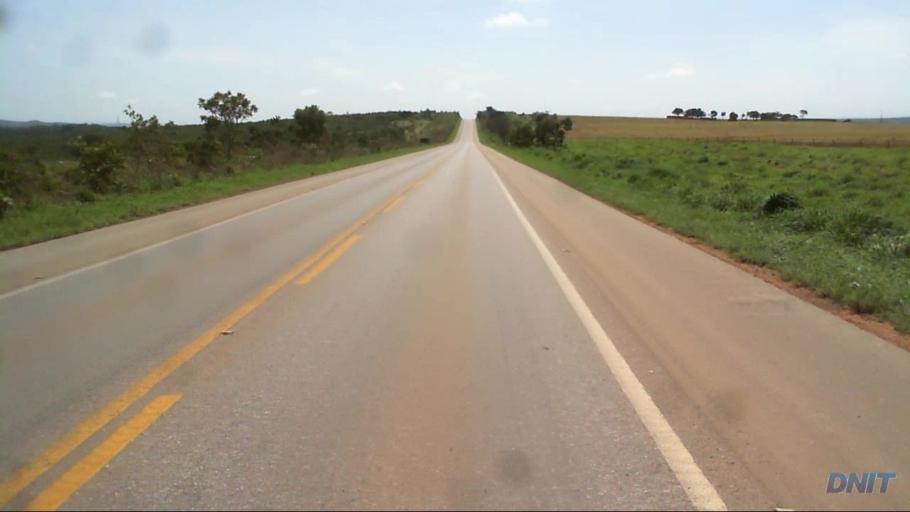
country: BR
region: Goias
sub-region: Barro Alto
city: Barro Alto
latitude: -15.2064
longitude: -48.7183
